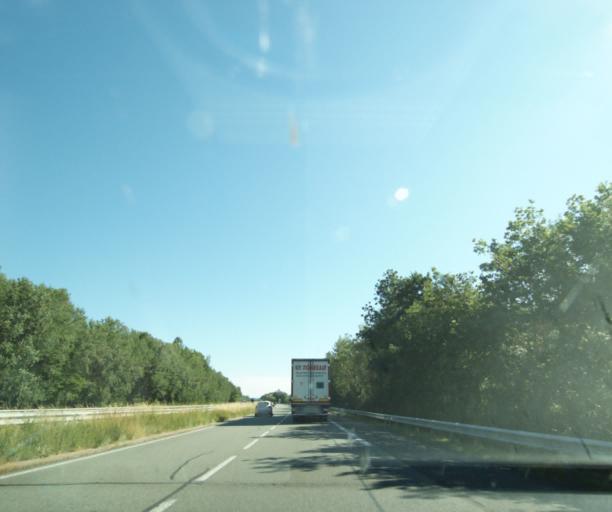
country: FR
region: Champagne-Ardenne
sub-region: Departement de la Haute-Marne
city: Avrecourt
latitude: 47.9712
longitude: 5.4943
